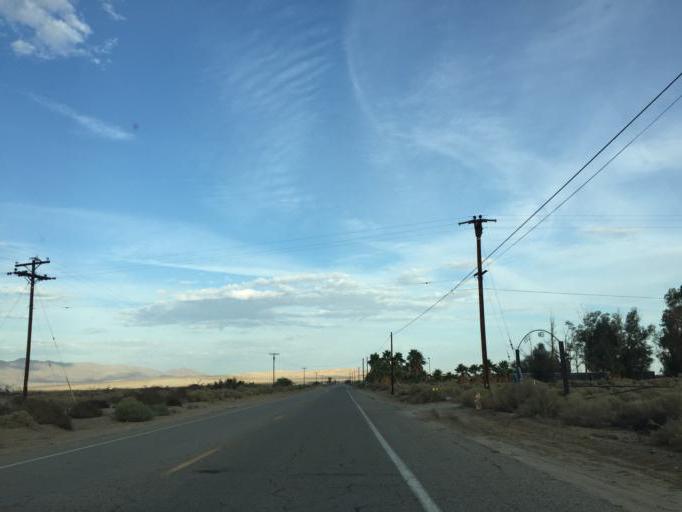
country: US
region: California
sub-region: San Diego County
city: Borrego Springs
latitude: 33.2569
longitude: -116.3400
